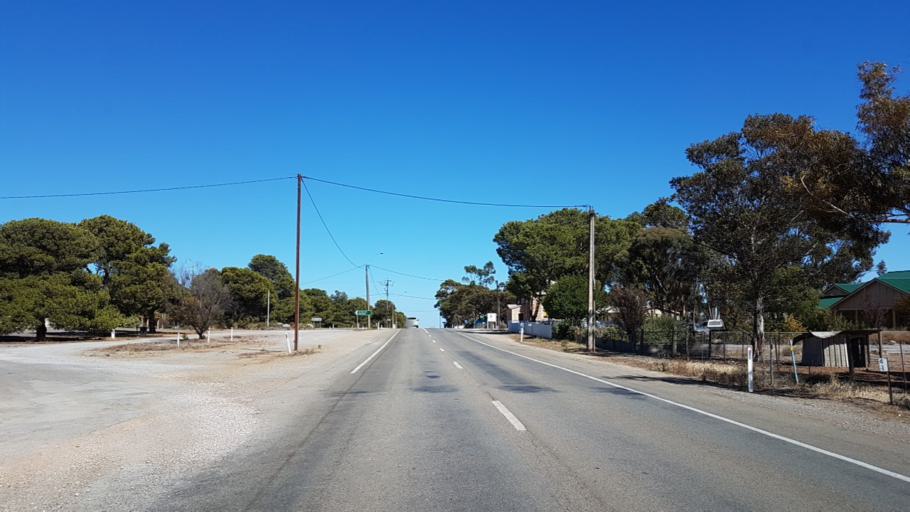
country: AU
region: South Australia
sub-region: Copper Coast
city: Kadina
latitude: -34.0598
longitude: 138.0379
